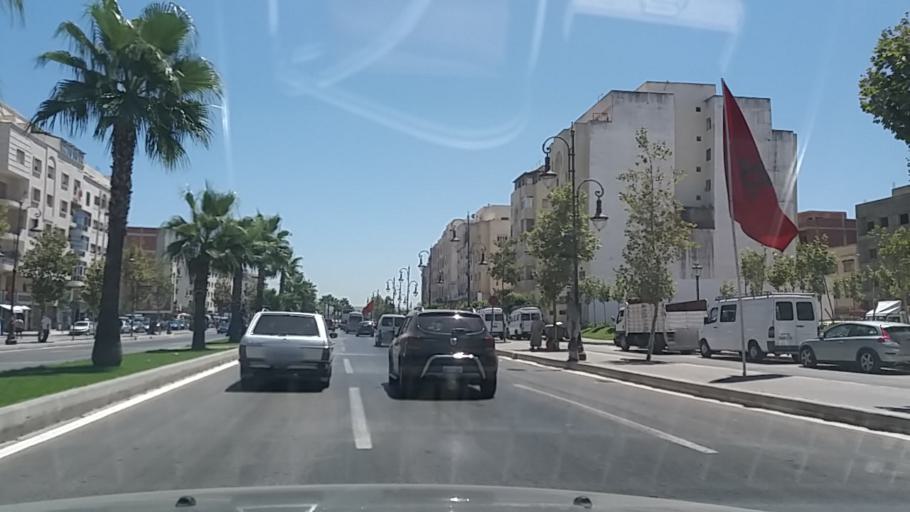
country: MA
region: Tanger-Tetouan
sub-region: Tanger-Assilah
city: Tangier
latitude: 35.7597
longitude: -5.7938
